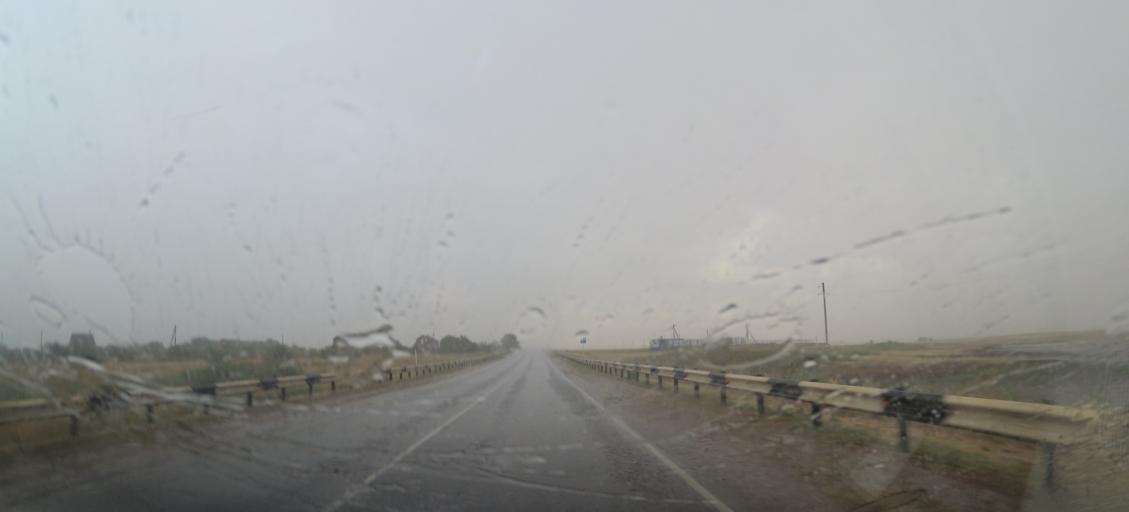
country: RU
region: Rostov
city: Proletarsk
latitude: 46.6801
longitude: 41.7113
